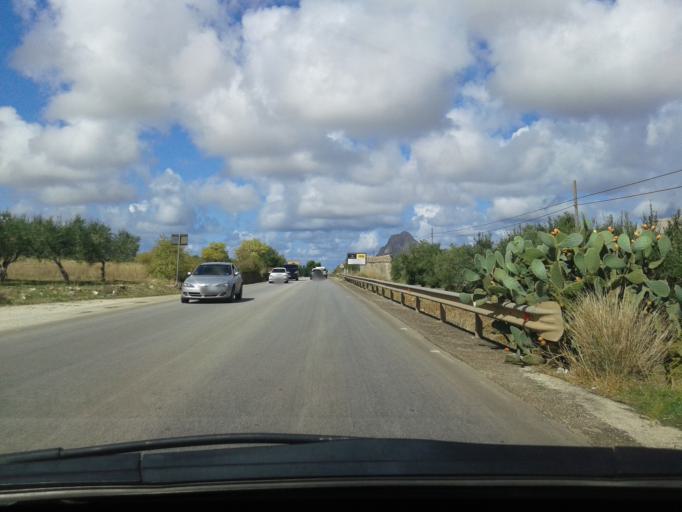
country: IT
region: Sicily
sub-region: Trapani
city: Castelluzzo
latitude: 38.0770
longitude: 12.7291
